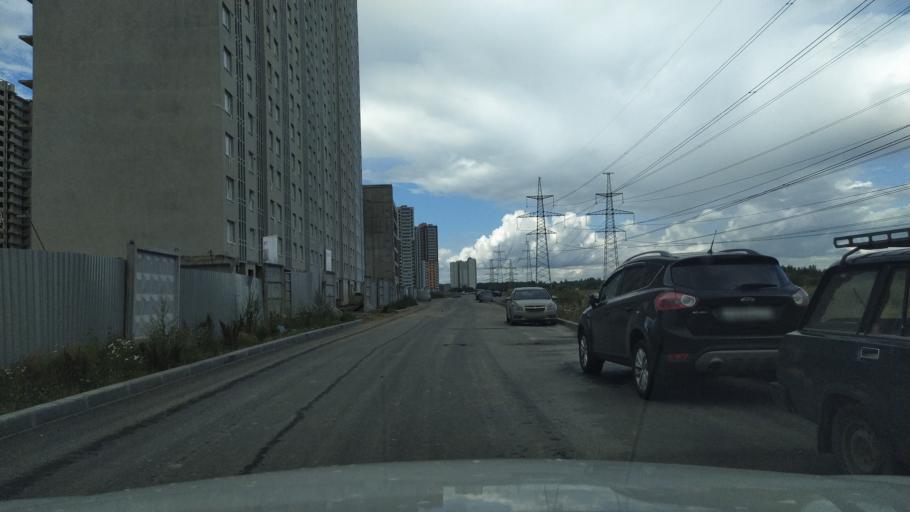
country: RU
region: St.-Petersburg
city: Krasnogvargeisky
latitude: 60.0021
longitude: 30.4830
